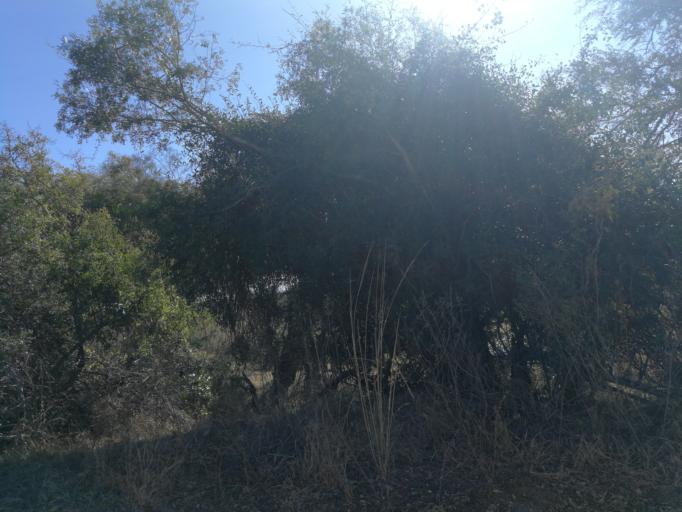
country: ZA
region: Limpopo
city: Thulamahashi
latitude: -24.9653
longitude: 31.6819
